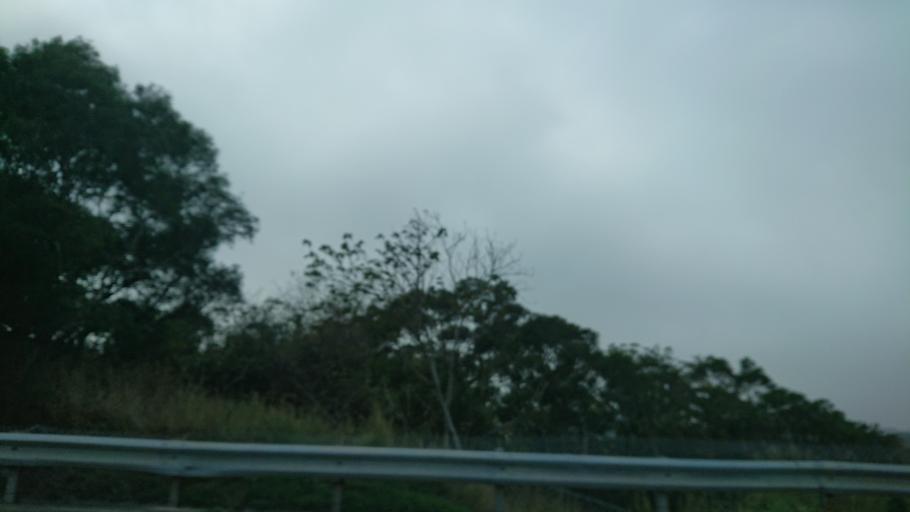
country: TW
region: Taiwan
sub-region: Miaoli
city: Miaoli
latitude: 24.4387
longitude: 120.6820
